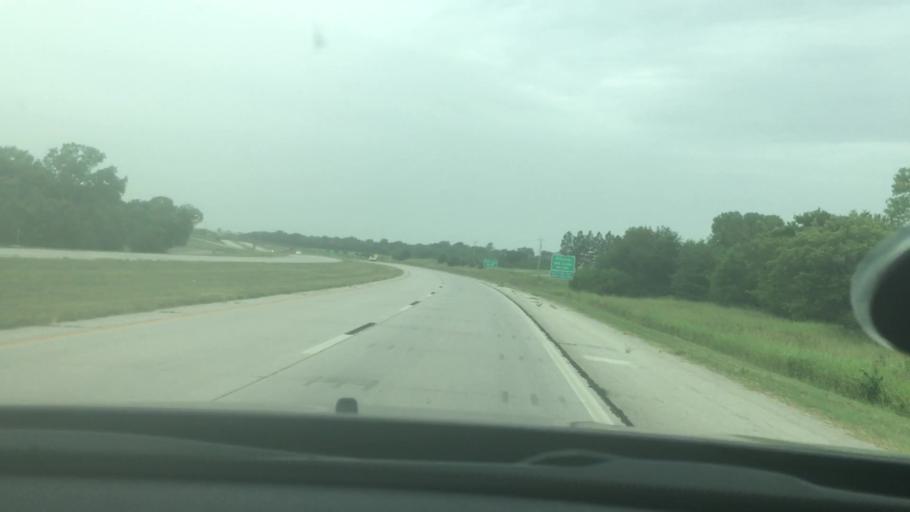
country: US
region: Oklahoma
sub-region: Pontotoc County
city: Ada
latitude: 34.7518
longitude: -96.6619
